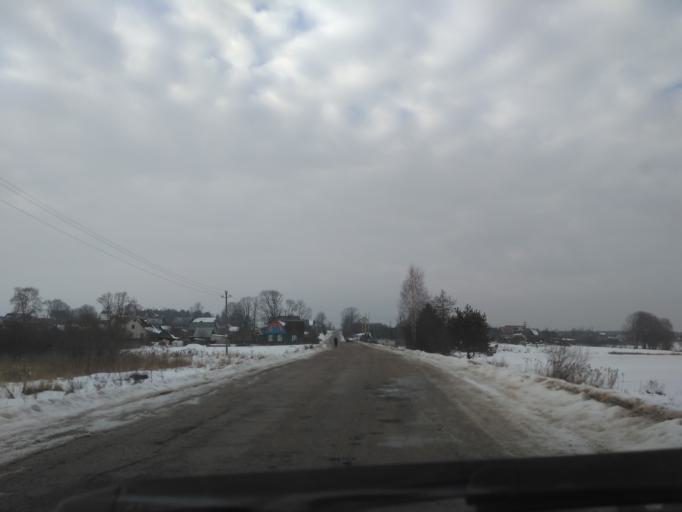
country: BY
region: Minsk
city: Zamostochcha
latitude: 53.8907
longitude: 27.9144
